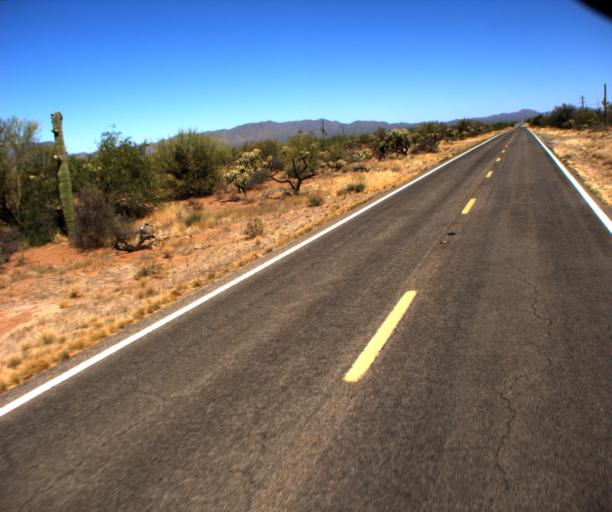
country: US
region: Arizona
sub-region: Pima County
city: Sells
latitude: 32.0499
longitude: -112.0252
